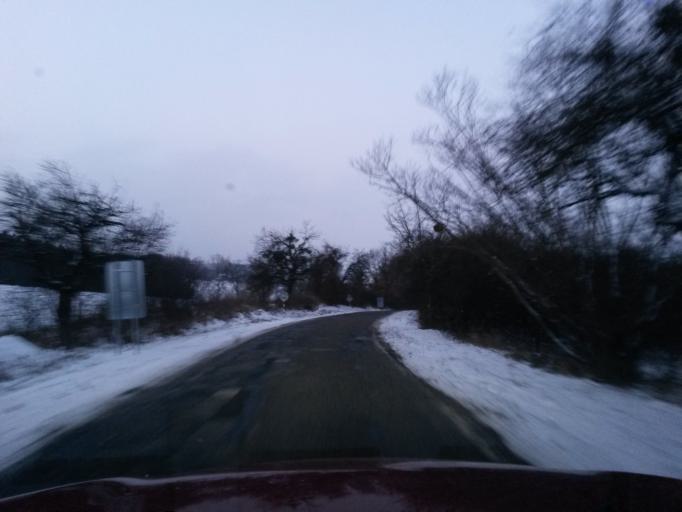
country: SK
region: Kosicky
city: Kosice
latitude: 48.7347
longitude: 21.3271
